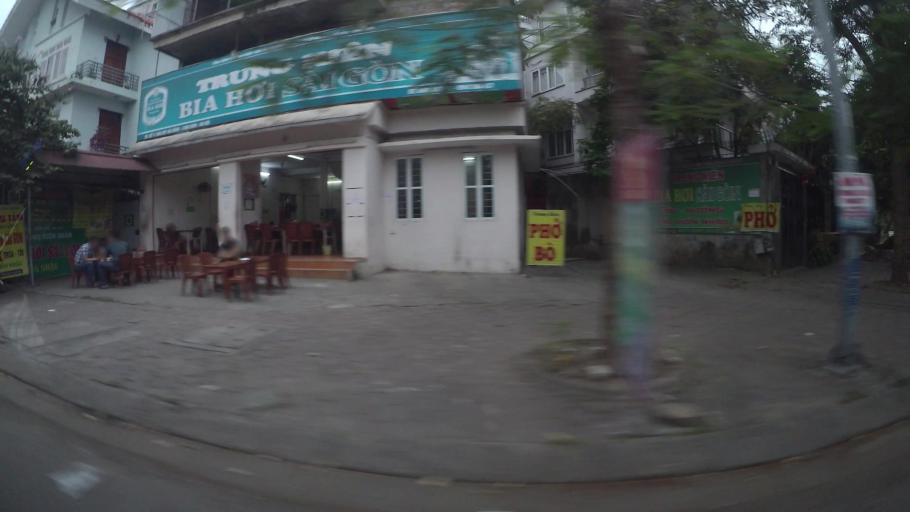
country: VN
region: Ha Noi
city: Trau Quy
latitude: 21.0381
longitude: 105.9046
